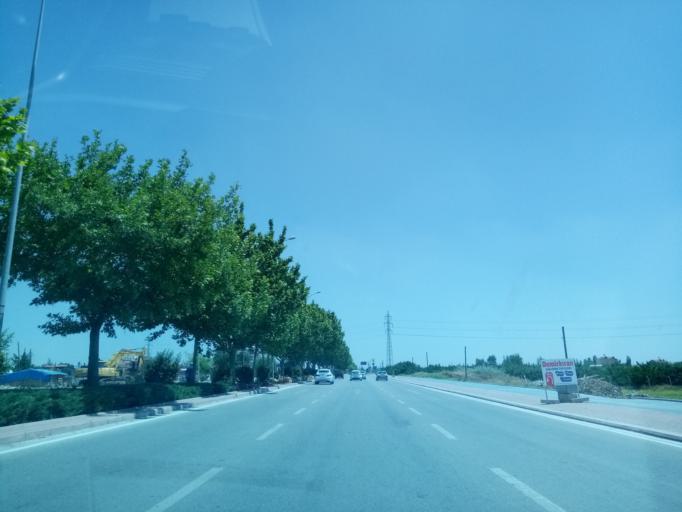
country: TR
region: Konya
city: Meram
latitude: 37.8266
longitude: 32.4718
